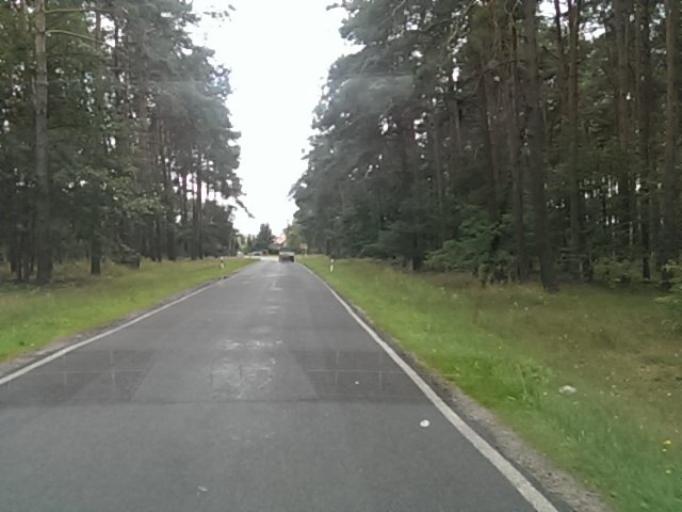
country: DE
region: Brandenburg
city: Borkheide
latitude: 52.1707
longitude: 12.8566
